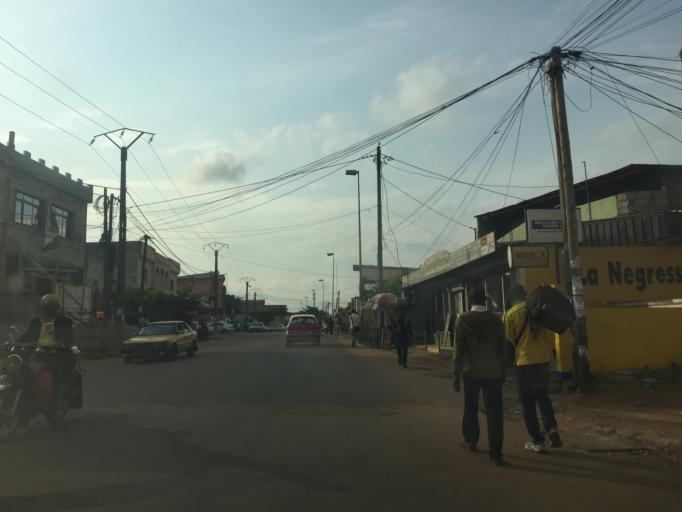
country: CM
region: Centre
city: Yaounde
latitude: 3.8791
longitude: 11.5243
